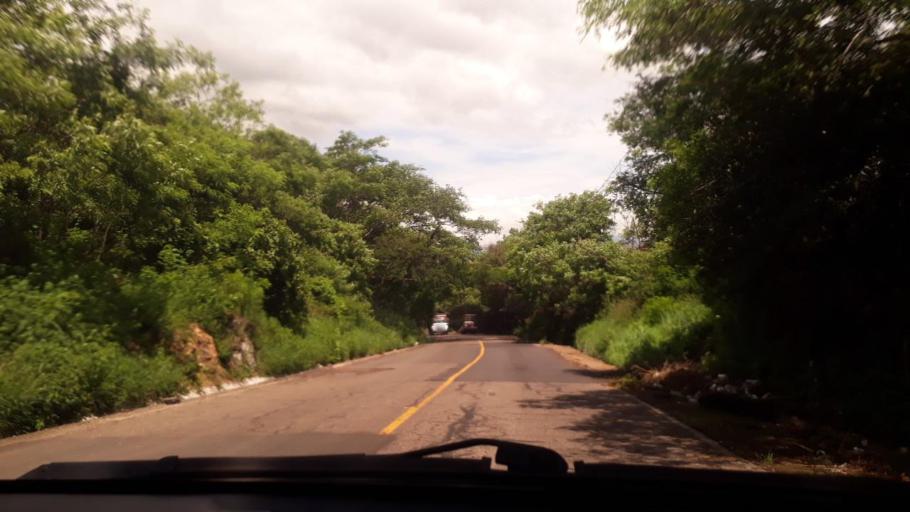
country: GT
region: Jutiapa
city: Jalpatagua
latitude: 14.1671
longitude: -90.0476
